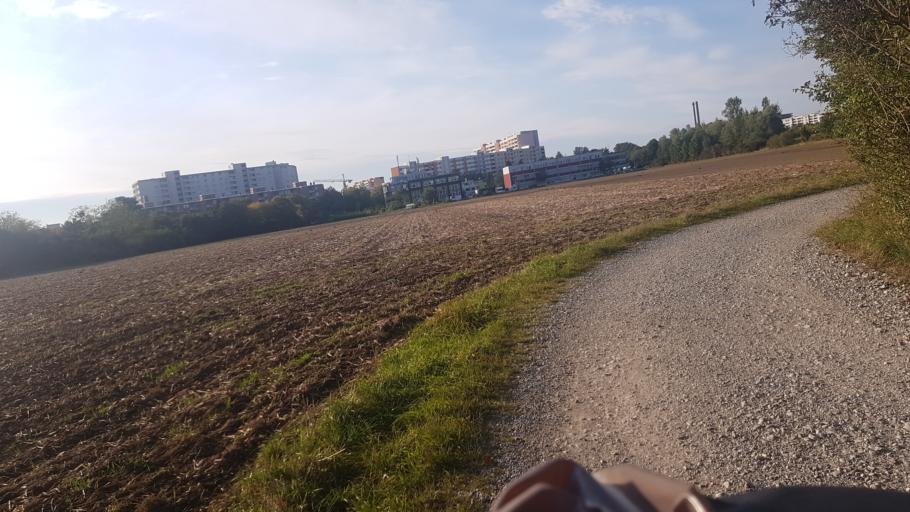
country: DE
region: Bavaria
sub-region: Upper Bavaria
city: Neubiberg
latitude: 48.0966
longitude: 11.6651
